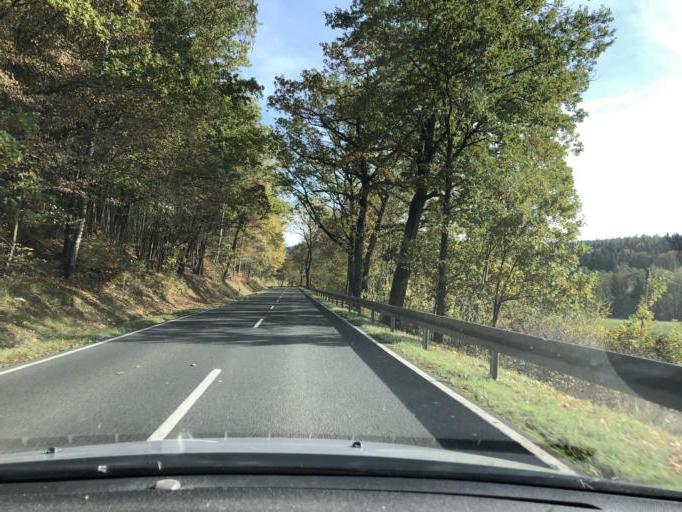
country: DE
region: Thuringia
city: Ehrenberg
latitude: 50.4887
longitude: 10.6784
